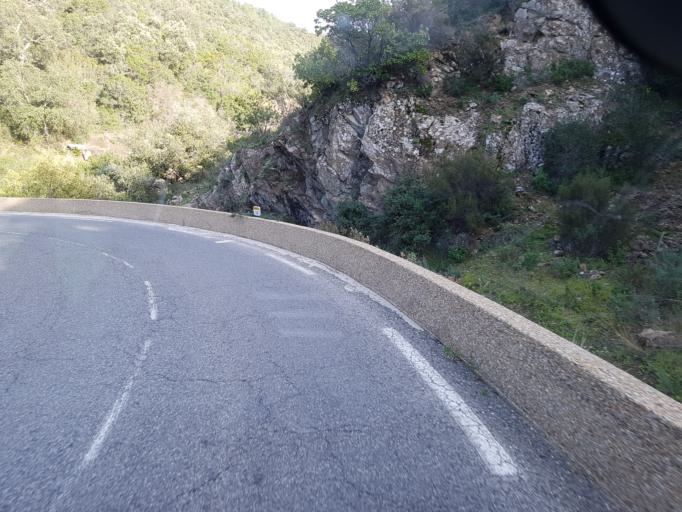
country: FR
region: Provence-Alpes-Cote d'Azur
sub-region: Departement du Var
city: La Garde-Freinet
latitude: 43.3331
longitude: 6.4497
